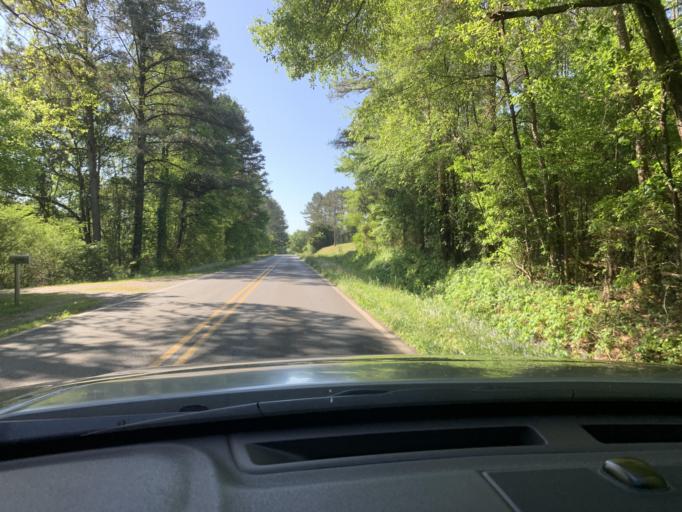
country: US
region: Georgia
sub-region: Polk County
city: Cedartown
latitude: 34.0385
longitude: -85.3018
